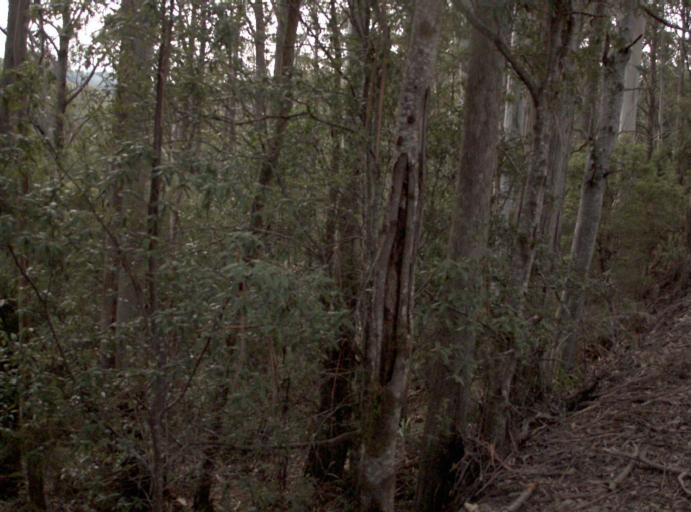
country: AU
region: Tasmania
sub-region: Dorset
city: Scottsdale
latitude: -41.2808
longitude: 147.3394
